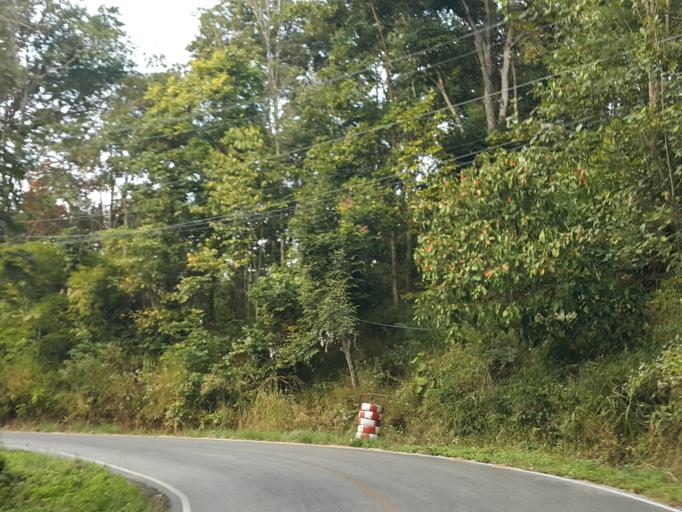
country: TH
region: Chiang Mai
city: Mae On
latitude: 18.8480
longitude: 99.2743
